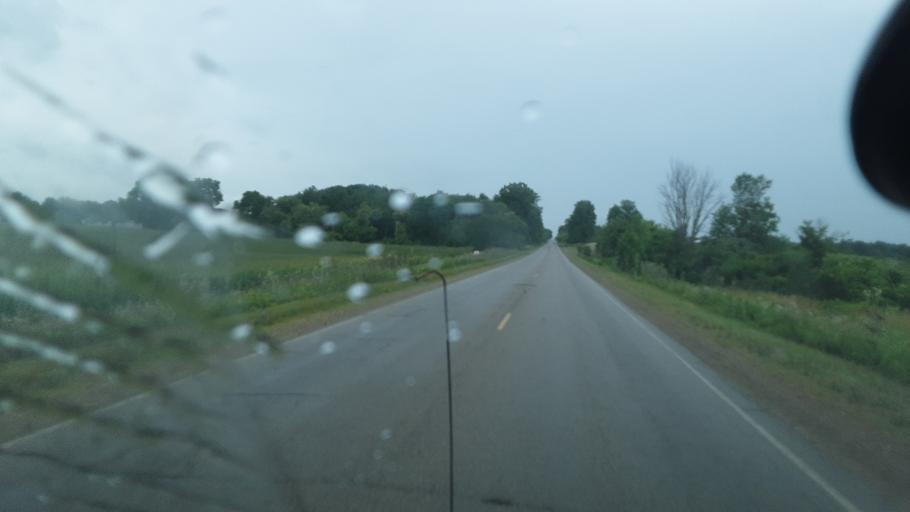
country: US
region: Michigan
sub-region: Hillsdale County
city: Reading
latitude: 41.7080
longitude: -84.7643
